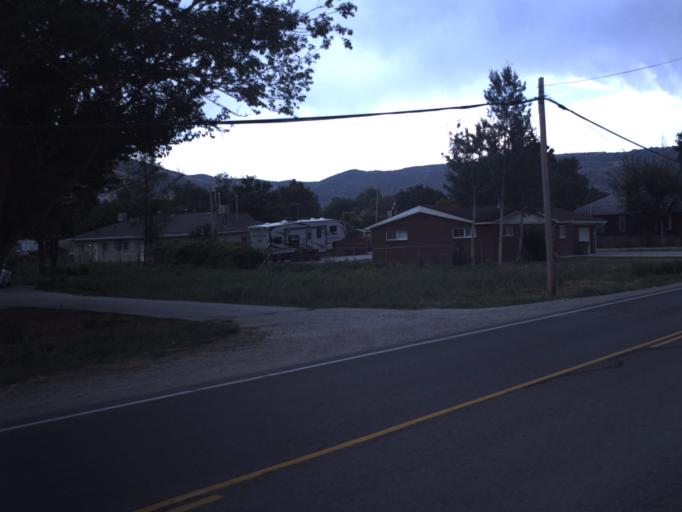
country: US
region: Utah
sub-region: Salt Lake County
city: Draper
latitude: 40.5321
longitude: -111.8712
